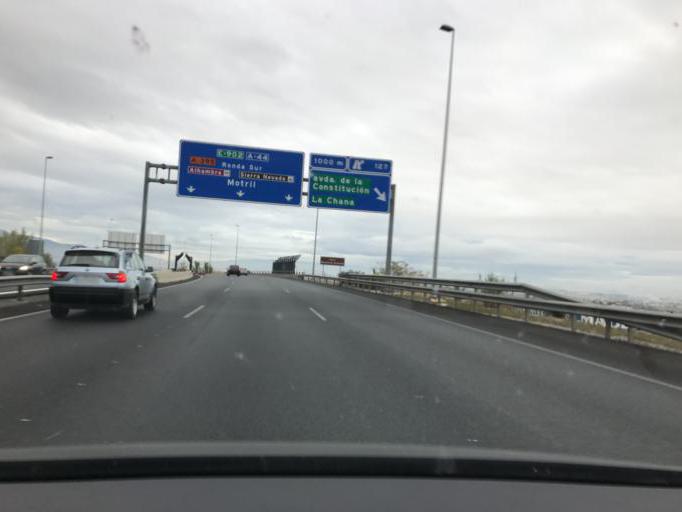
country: ES
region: Andalusia
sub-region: Provincia de Granada
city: Maracena
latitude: 37.1914
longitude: -3.6333
